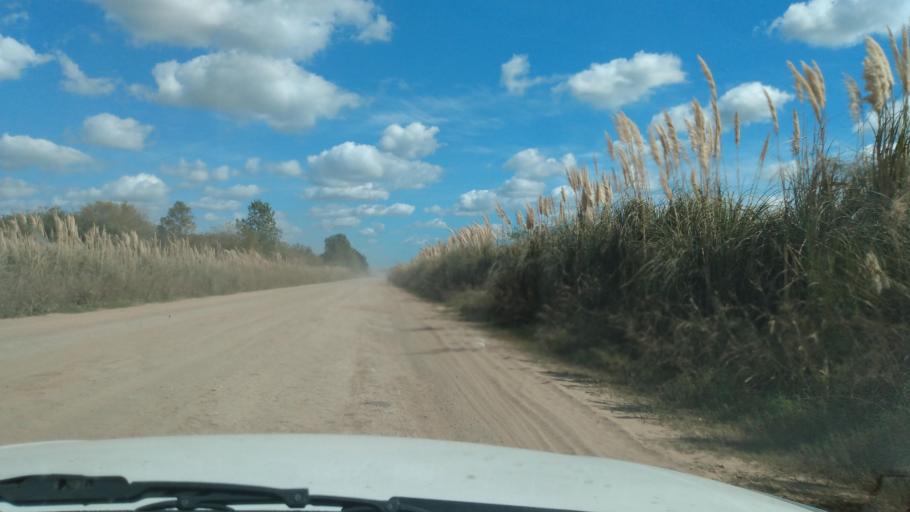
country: AR
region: Buenos Aires
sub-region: Partido de Navarro
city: Navarro
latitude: -34.9996
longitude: -59.3362
